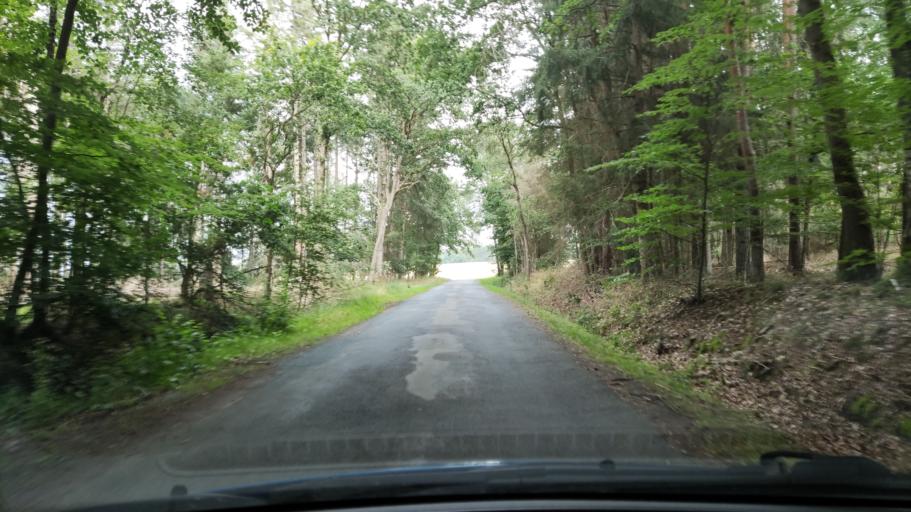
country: DE
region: Lower Saxony
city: Schnega
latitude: 52.9295
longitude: 10.8807
